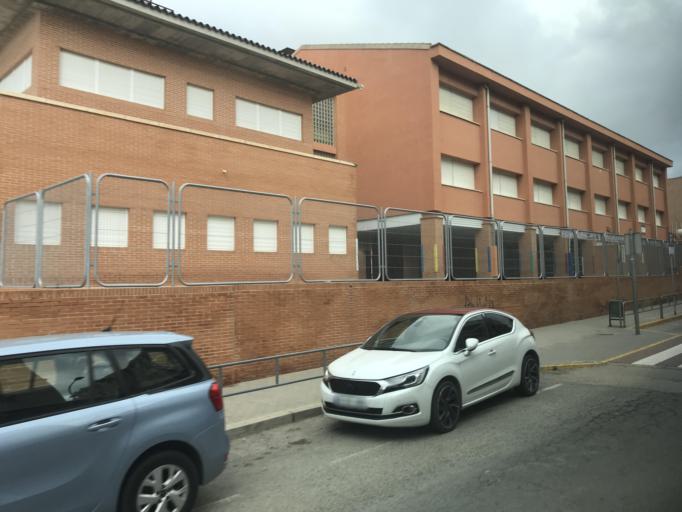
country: ES
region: Valencia
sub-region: Provincia de Alicante
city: Guardamar del Segura
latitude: 38.0862
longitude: -0.6553
